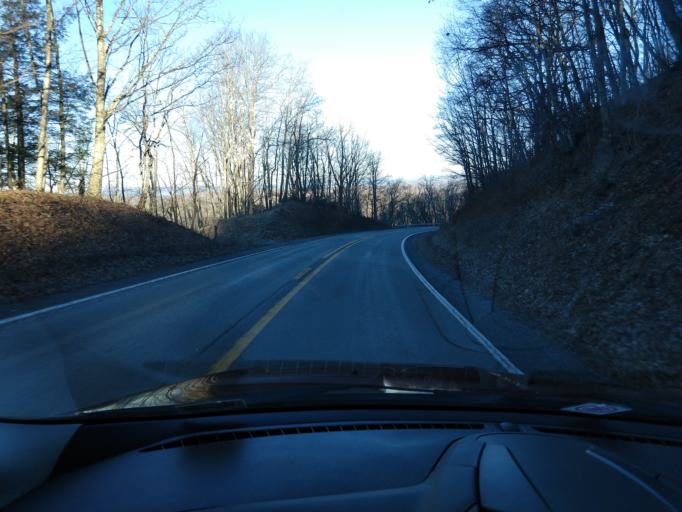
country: US
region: Virginia
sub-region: Highland County
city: Monterey
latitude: 38.4833
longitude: -79.7025
